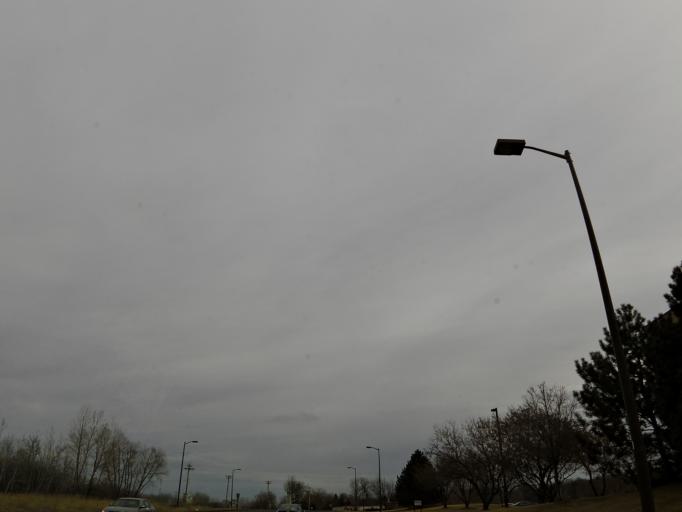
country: US
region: Minnesota
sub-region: Scott County
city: Savage
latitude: 44.7719
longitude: -93.3811
